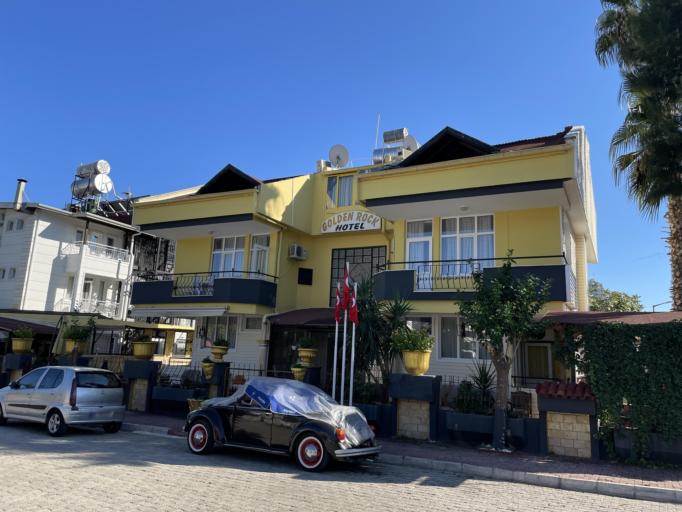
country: TR
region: Antalya
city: Kemer
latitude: 36.6023
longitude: 30.5639
